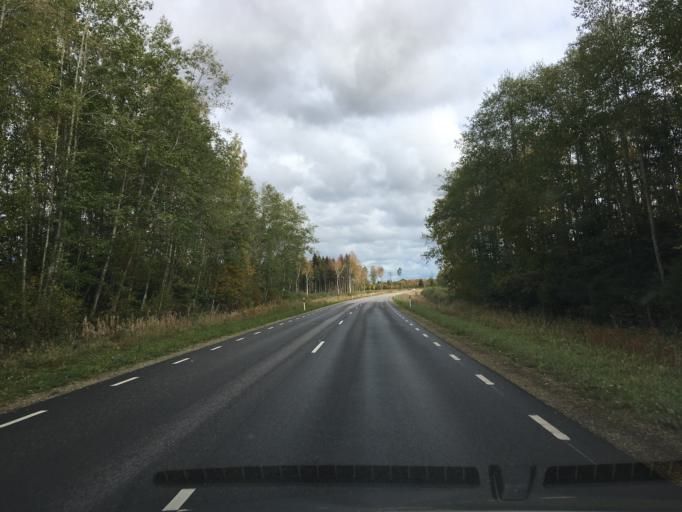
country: EE
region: Harju
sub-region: Anija vald
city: Kehra
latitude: 59.2430
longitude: 25.2981
